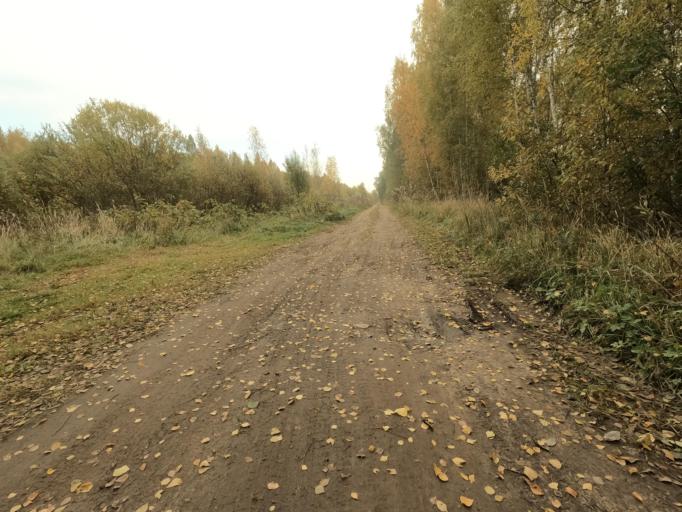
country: RU
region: Novgorod
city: Pankovka
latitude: 58.8708
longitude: 30.8973
